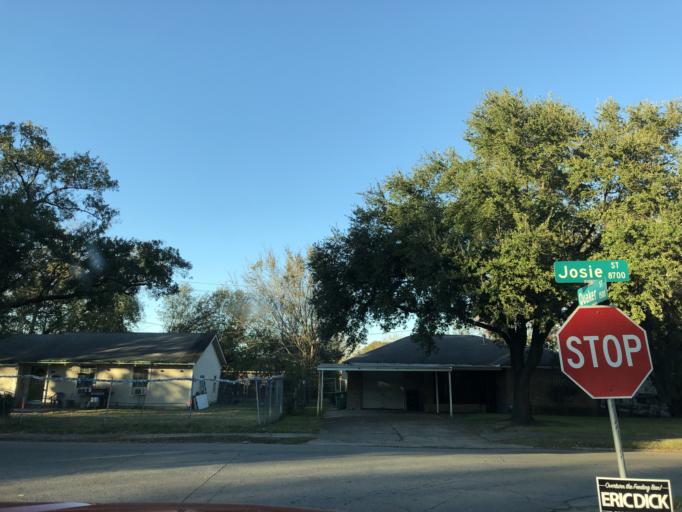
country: US
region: Texas
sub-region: Harris County
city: Jacinto City
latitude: 29.7625
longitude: -95.2674
